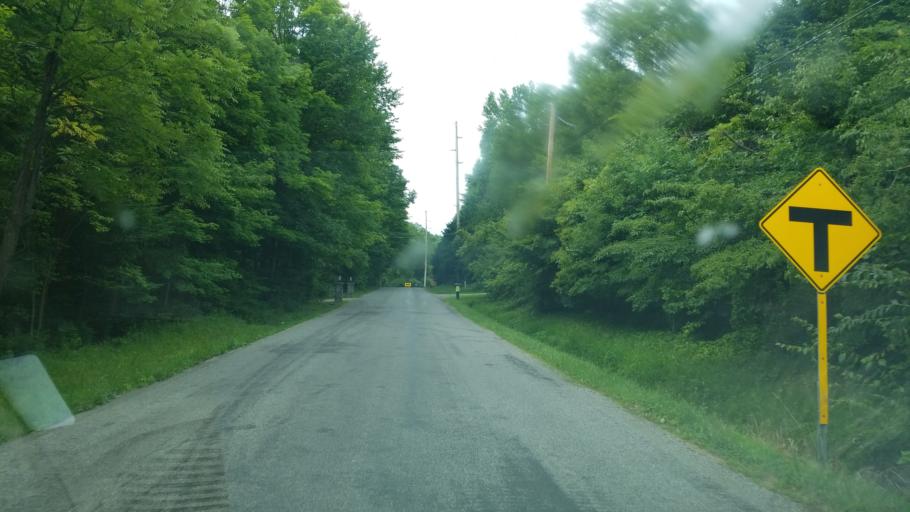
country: US
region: Ohio
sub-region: Ashland County
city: Ashland
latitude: 40.8445
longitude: -82.2890
